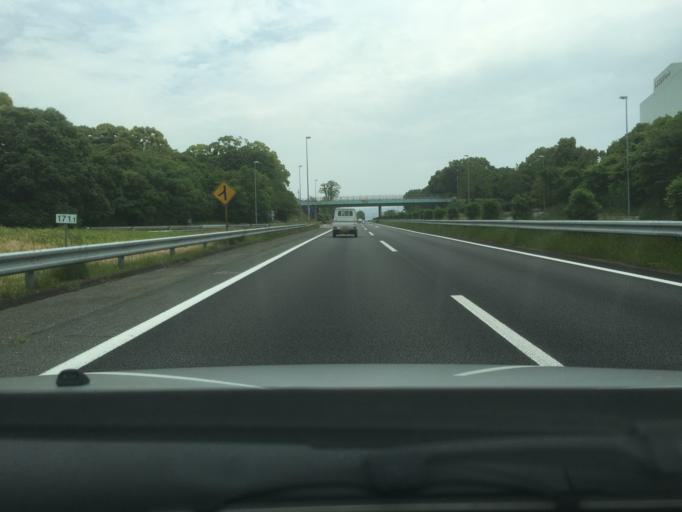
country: JP
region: Kumamoto
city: Kumamoto
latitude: 32.8359
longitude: 130.7786
